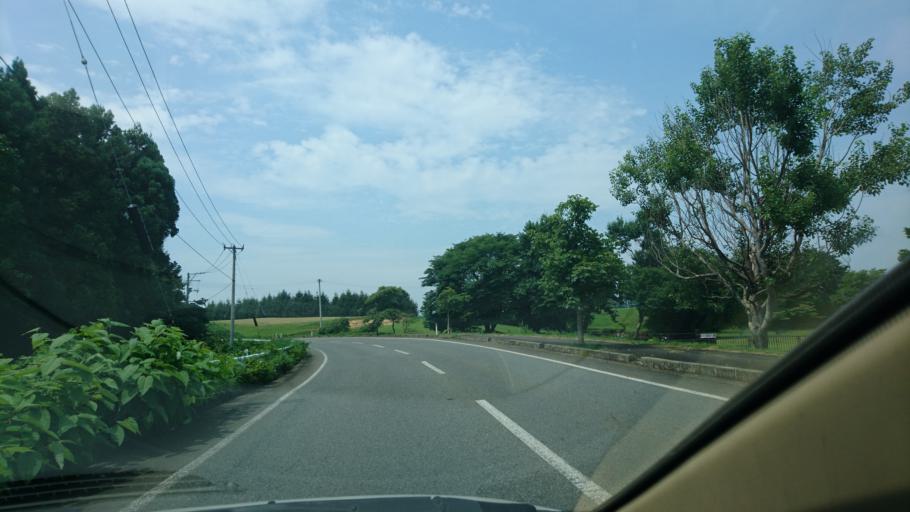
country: JP
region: Iwate
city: Kitakami
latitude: 39.2549
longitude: 141.0901
